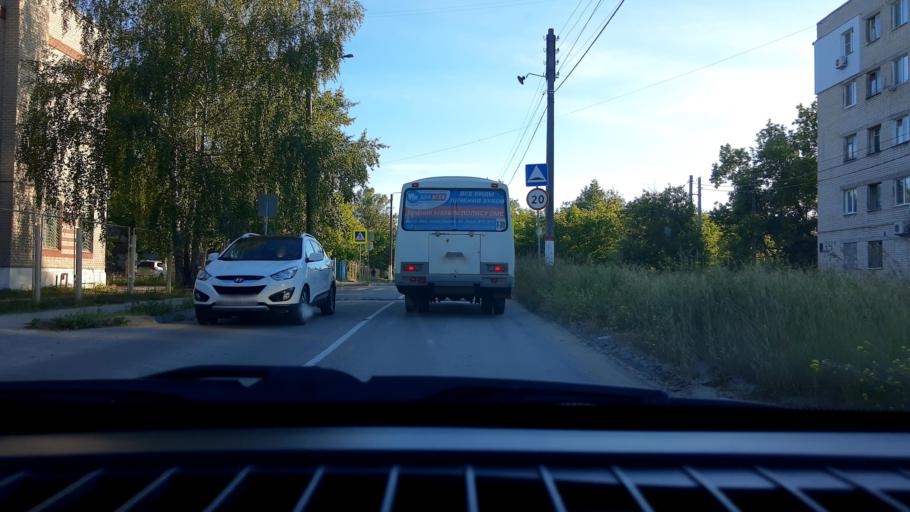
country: RU
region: Nizjnij Novgorod
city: Dzerzhinsk
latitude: 56.2438
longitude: 43.4892
